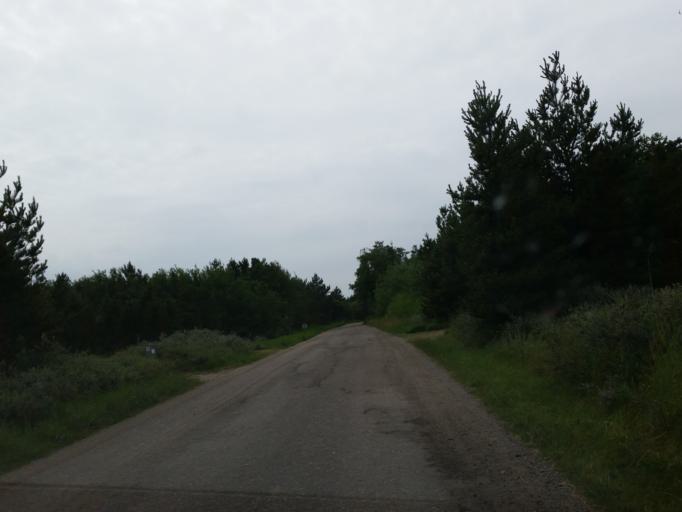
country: DE
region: Schleswig-Holstein
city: List
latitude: 55.1571
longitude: 8.5248
